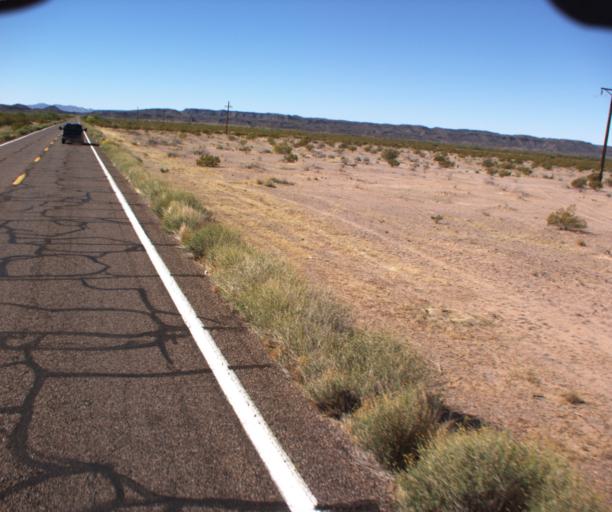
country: US
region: Arizona
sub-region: Pima County
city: Ajo
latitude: 32.6043
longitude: -112.8696
